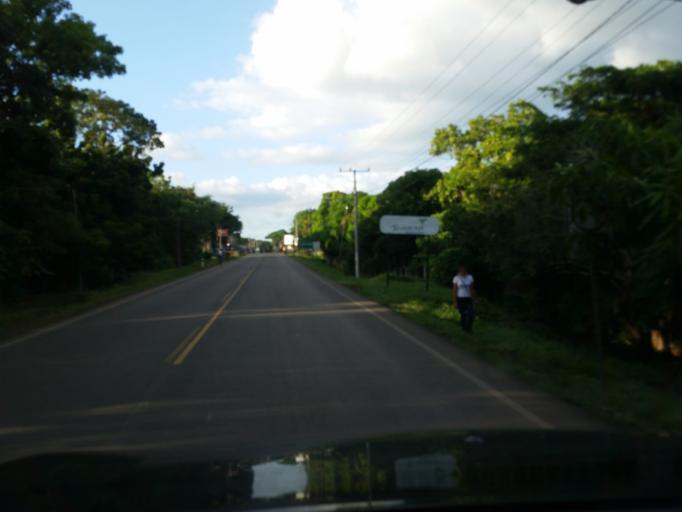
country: NI
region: Granada
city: Nandaime
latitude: 11.7742
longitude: -86.0522
